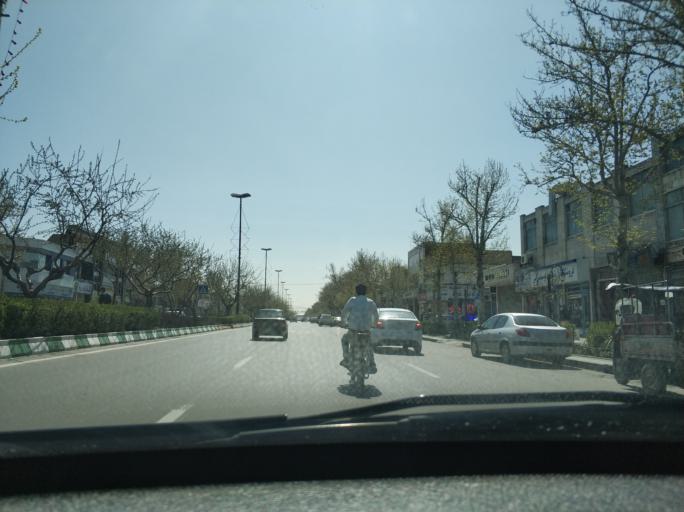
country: IR
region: Razavi Khorasan
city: Mashhad
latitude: 36.2654
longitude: 59.6012
